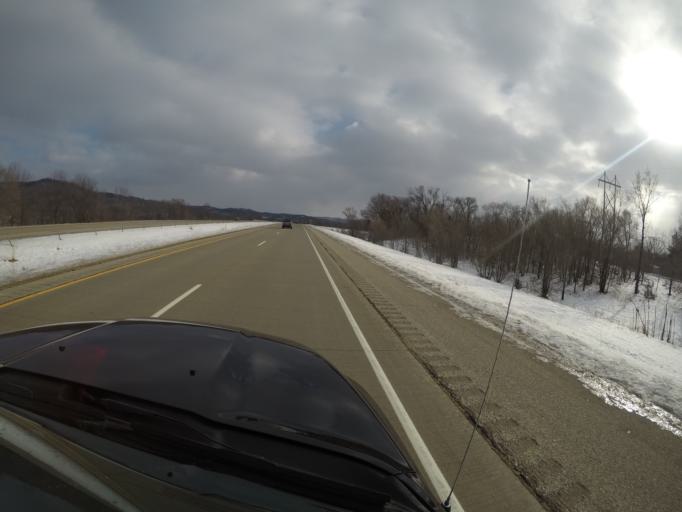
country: US
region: Wisconsin
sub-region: La Crosse County
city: Holmen
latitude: 43.9435
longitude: -91.2597
